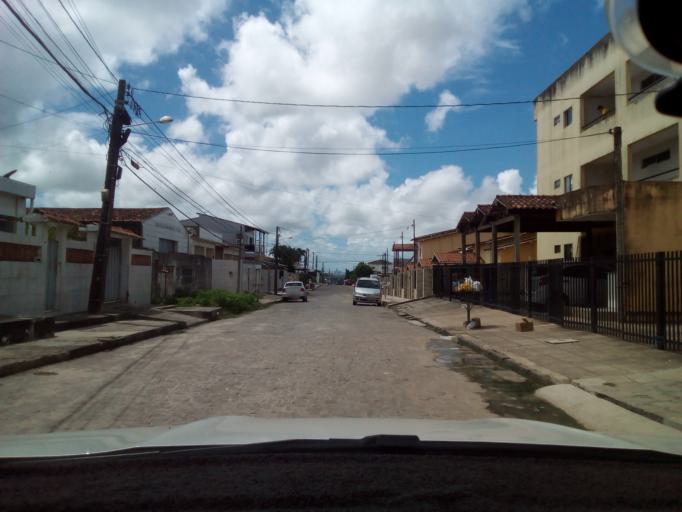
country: BR
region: Paraiba
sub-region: Bayeux
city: Bayeux
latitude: -7.1383
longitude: -34.9386
